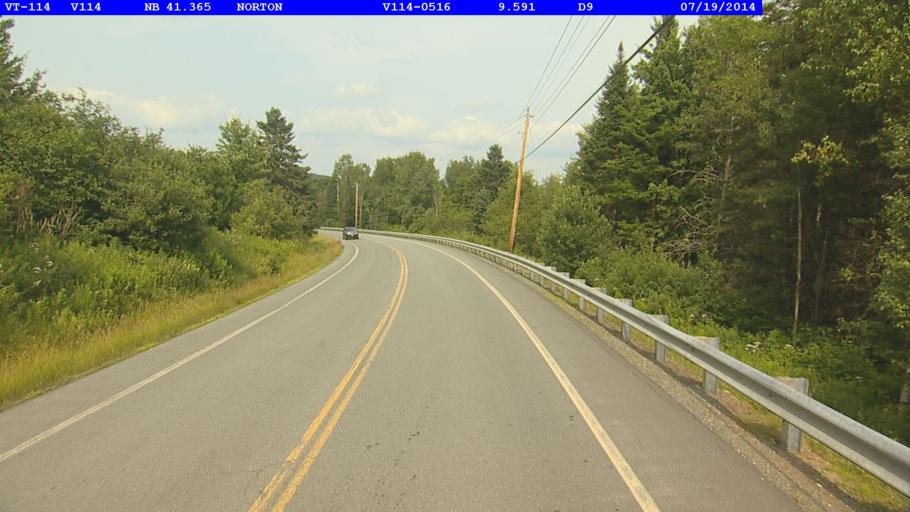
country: CA
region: Quebec
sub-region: Estrie
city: Coaticook
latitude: 44.9957
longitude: -71.7139
